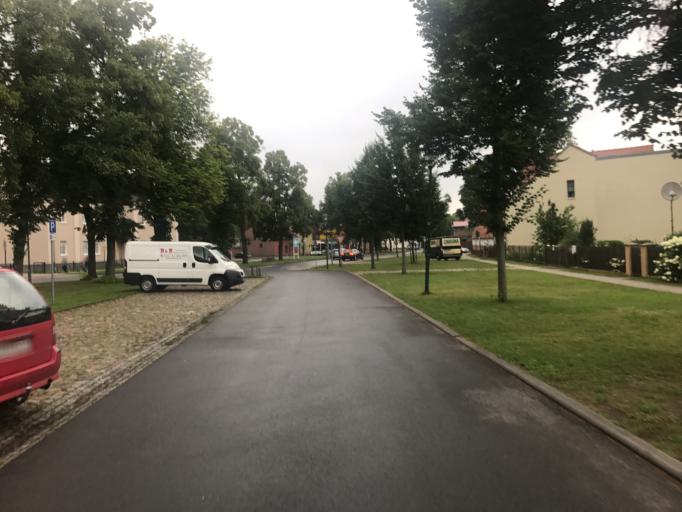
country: DE
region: Brandenburg
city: Melchow
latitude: 52.8493
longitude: 13.6838
